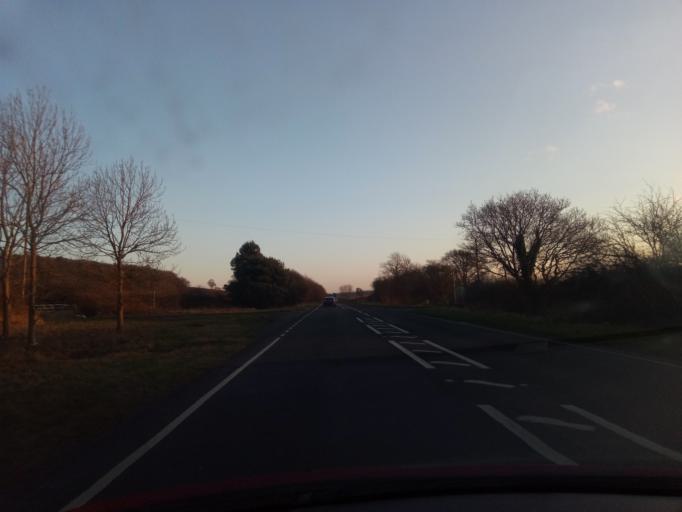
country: GB
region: England
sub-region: Nottinghamshire
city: Farnsfield
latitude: 53.0484
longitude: -1.0643
